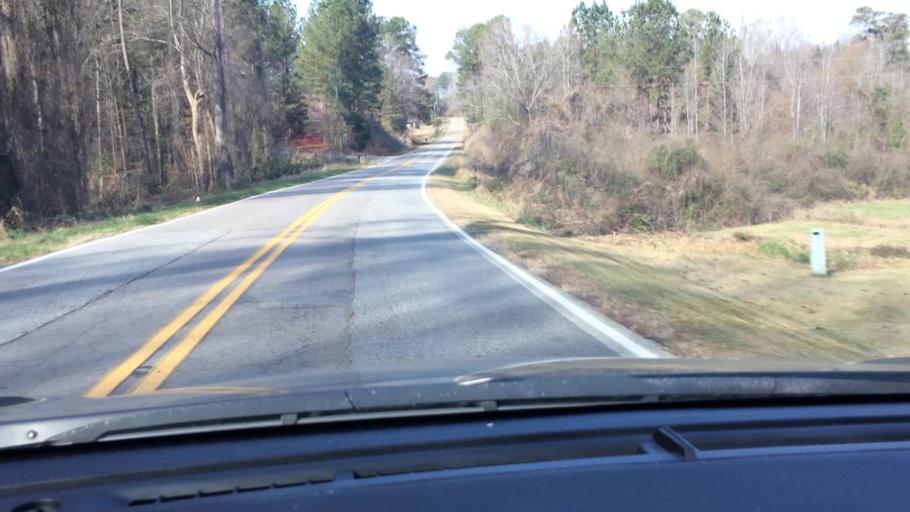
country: US
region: South Carolina
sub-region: Newberry County
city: Newberry
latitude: 34.2594
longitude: -81.5668
